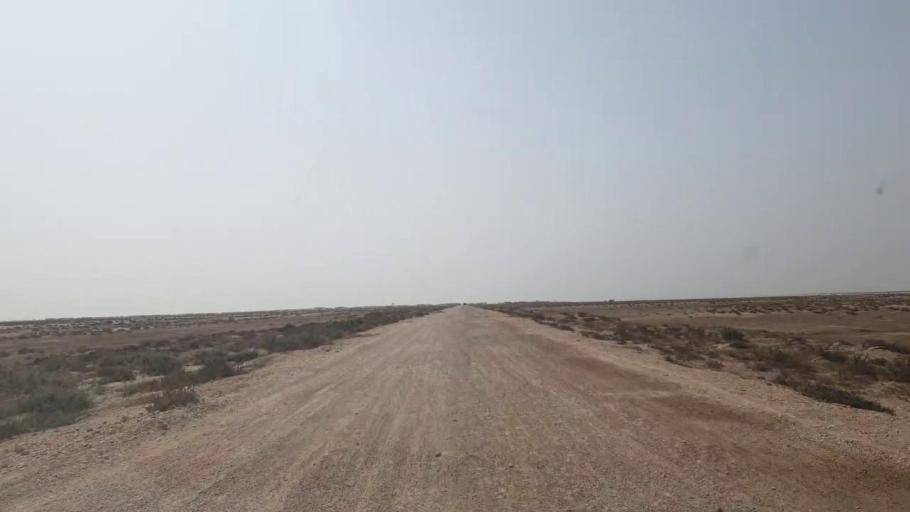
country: PK
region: Sindh
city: Jati
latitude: 24.3529
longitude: 68.5938
